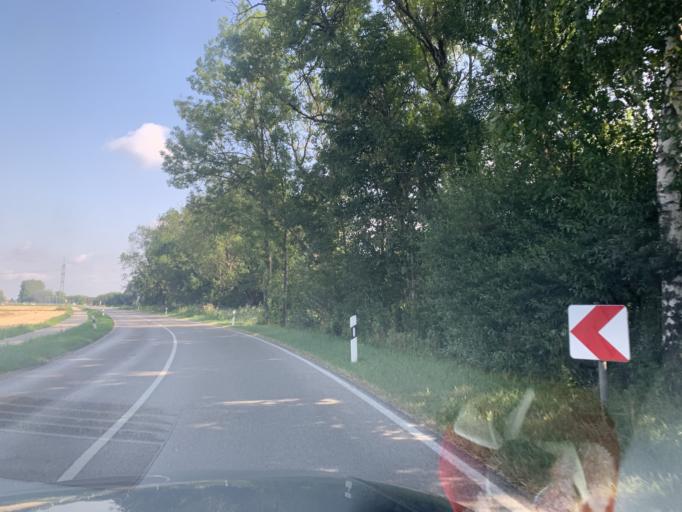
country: DE
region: Bavaria
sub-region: Swabia
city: Mering
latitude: 48.2798
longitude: 10.9850
